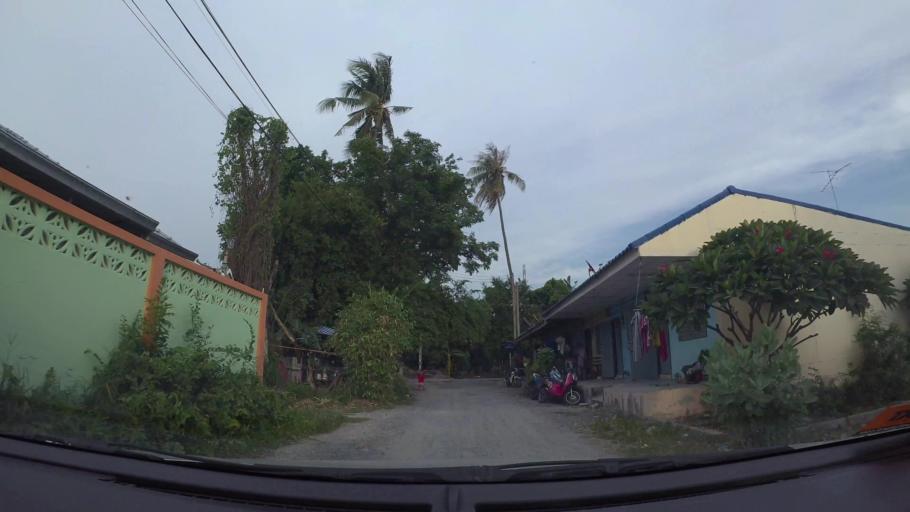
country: TH
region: Chon Buri
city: Chon Buri
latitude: 13.3369
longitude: 100.9860
